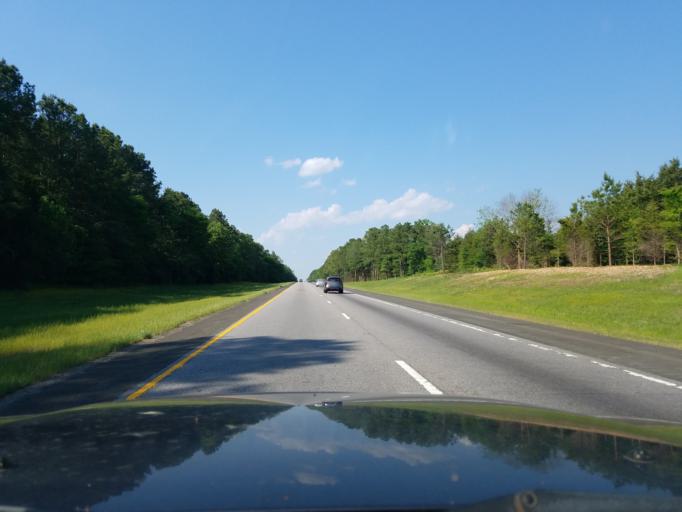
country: US
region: North Carolina
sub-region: Granville County
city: Butner
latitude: 36.0990
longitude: -78.7567
